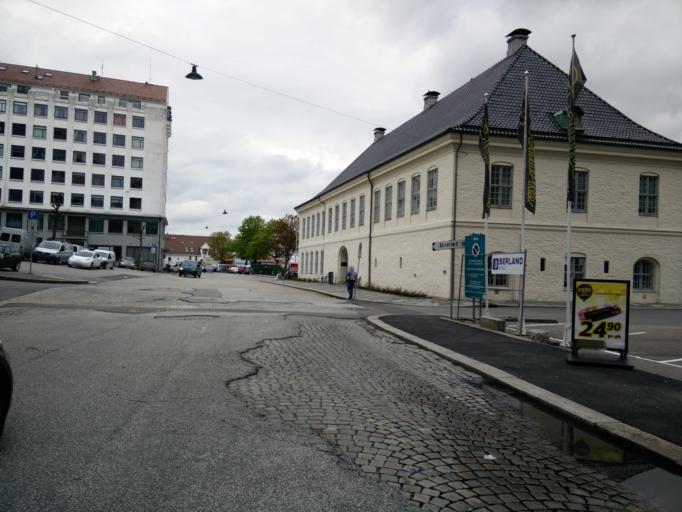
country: NO
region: Hordaland
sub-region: Bergen
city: Bergen
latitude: 60.3984
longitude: 5.3111
